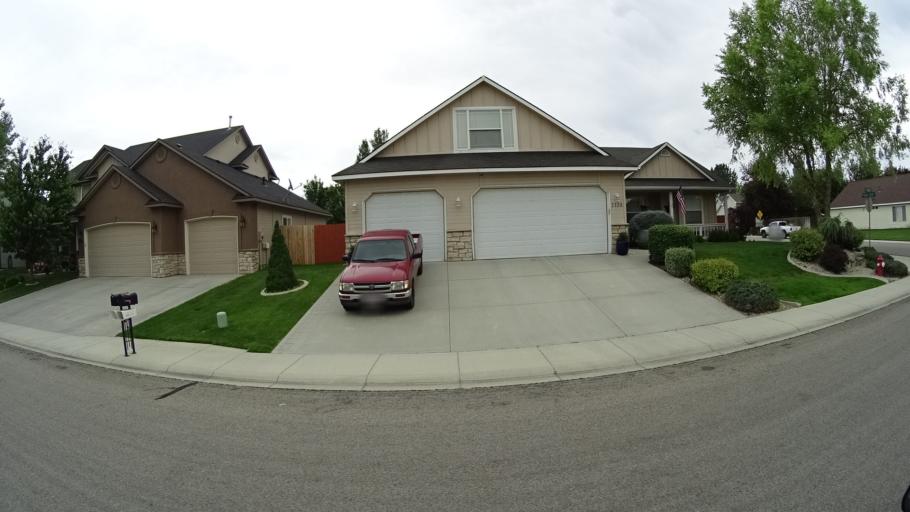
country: US
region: Idaho
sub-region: Ada County
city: Meridian
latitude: 43.5840
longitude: -116.3248
